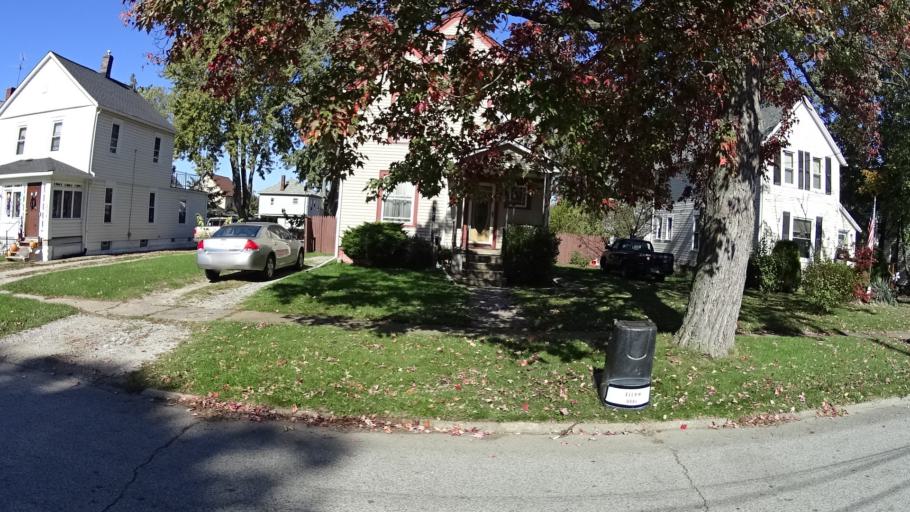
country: US
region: Ohio
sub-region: Lorain County
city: Lorain
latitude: 41.4441
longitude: -82.1666
